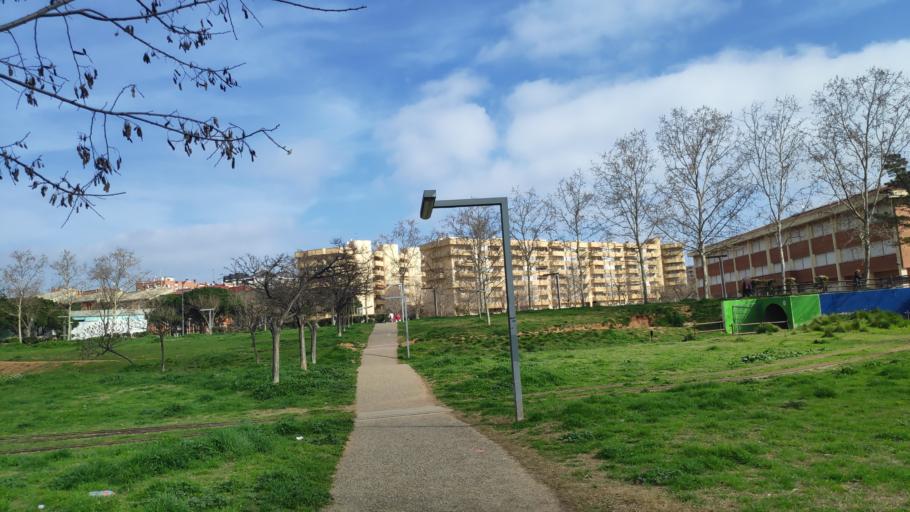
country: ES
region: Catalonia
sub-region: Provincia de Barcelona
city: Sant Quirze del Valles
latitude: 41.5521
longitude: 2.0851
